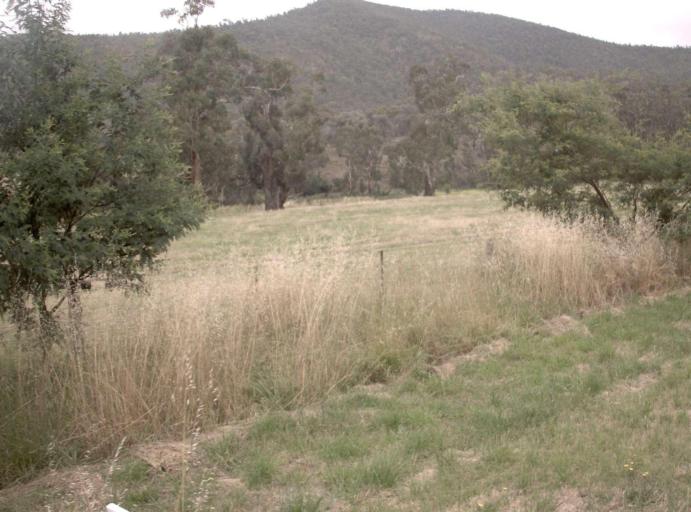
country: AU
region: Victoria
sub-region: Wellington
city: Heyfield
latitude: -37.7009
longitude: 146.6528
